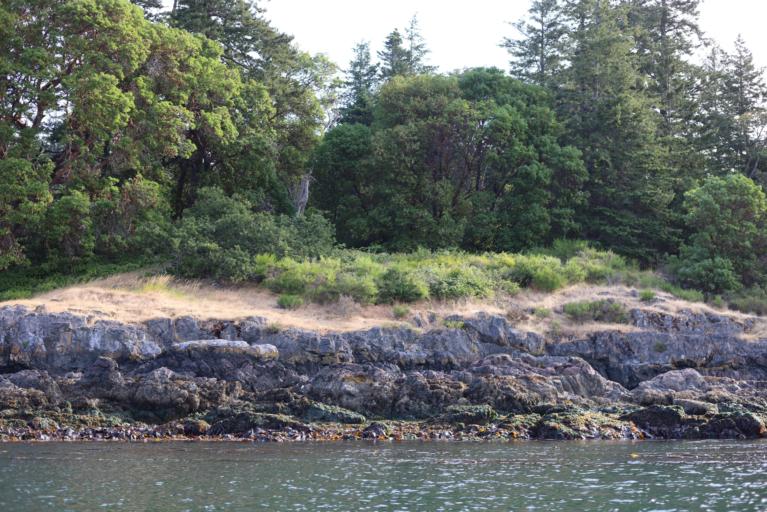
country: CA
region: British Columbia
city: Metchosin
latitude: 48.3408
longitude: -123.5553
